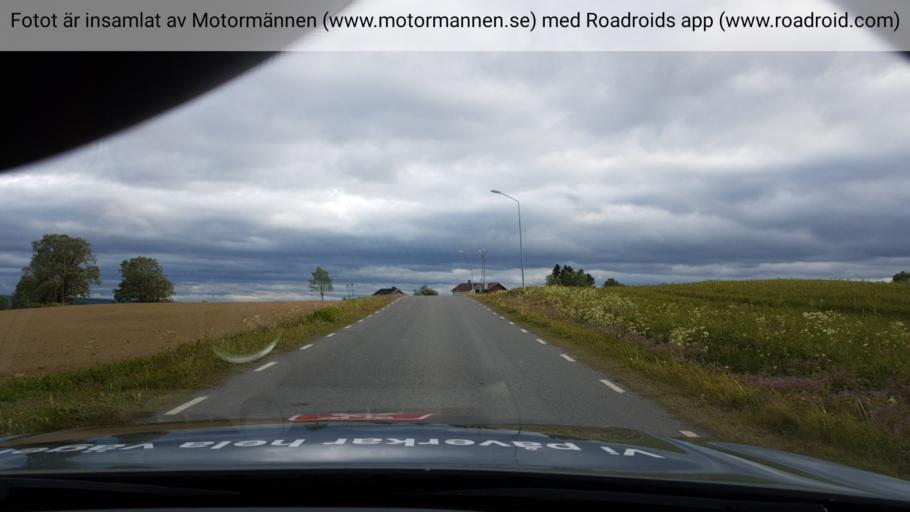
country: SE
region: Jaemtland
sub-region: OEstersunds Kommun
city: Lit
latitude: 63.6149
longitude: 15.0029
